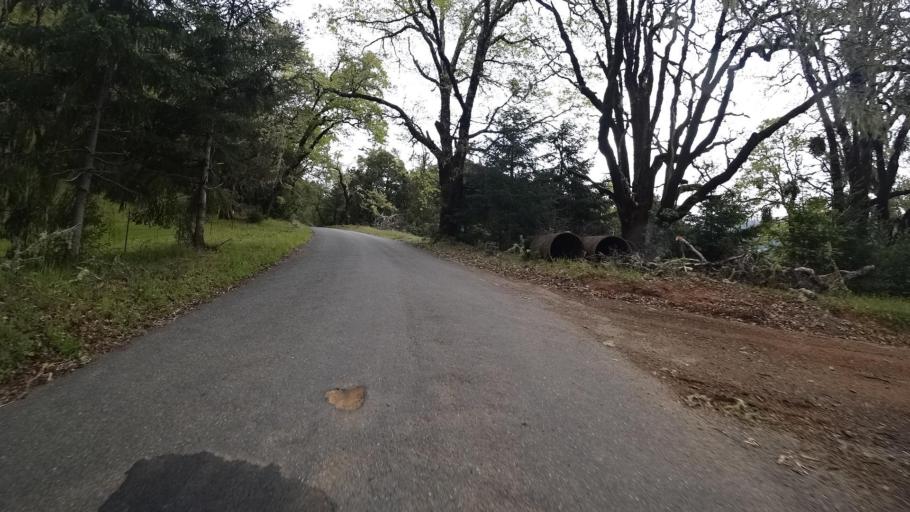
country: US
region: California
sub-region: Humboldt County
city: Redway
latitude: 40.1542
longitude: -123.5573
